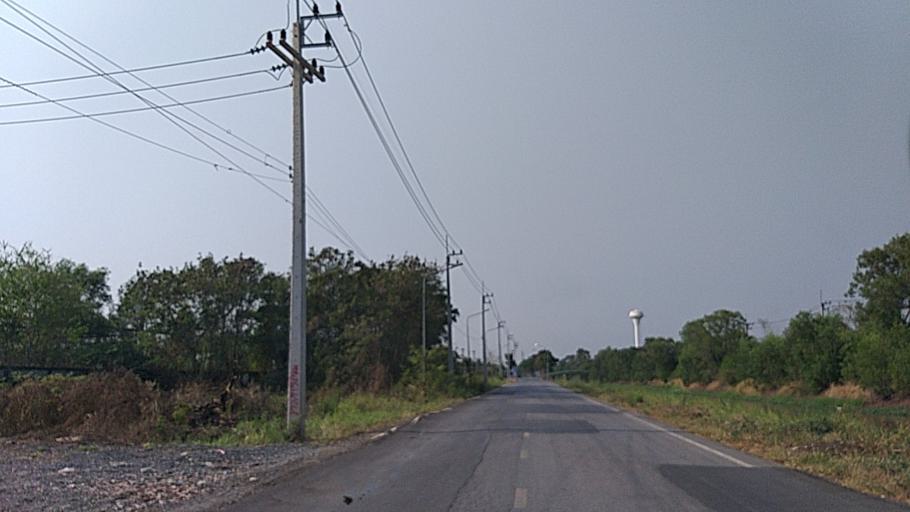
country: TH
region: Pathum Thani
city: Thanyaburi
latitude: 13.9965
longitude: 100.7068
